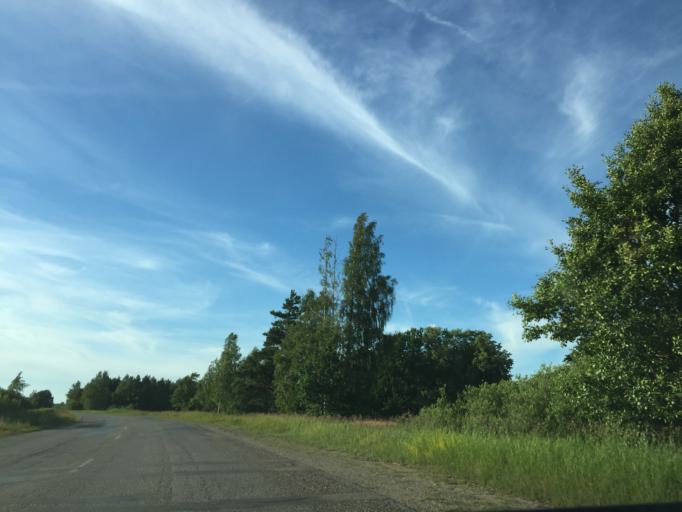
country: LV
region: Ventspils
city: Ventspils
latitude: 57.3448
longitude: 21.5690
